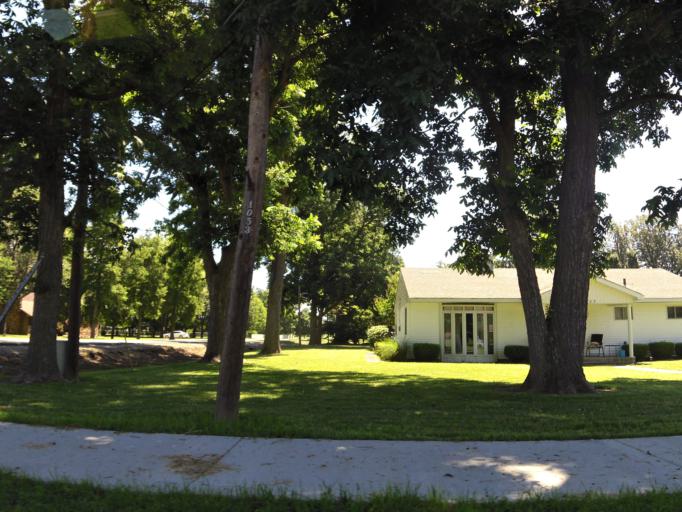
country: US
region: Missouri
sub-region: New Madrid County
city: New Madrid
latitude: 36.5956
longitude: -89.5273
